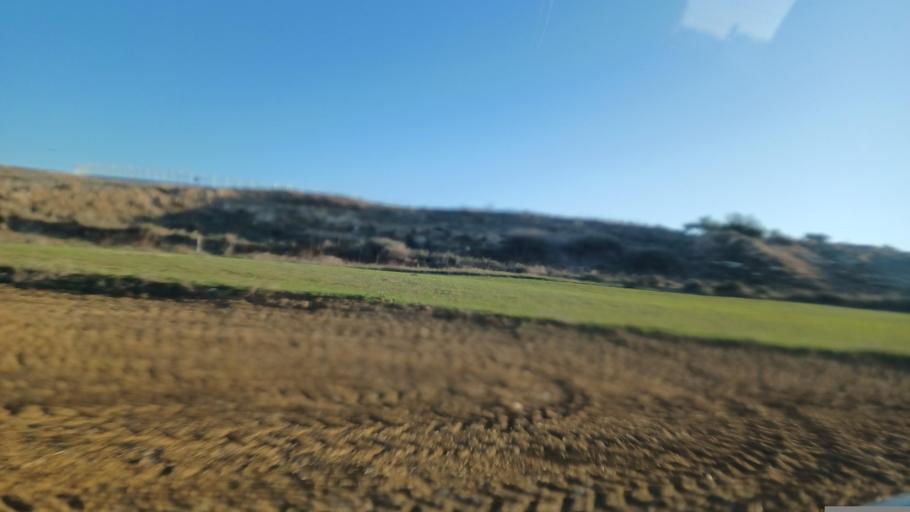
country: CY
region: Lefkosia
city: Mammari
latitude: 35.1541
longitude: 33.2635
